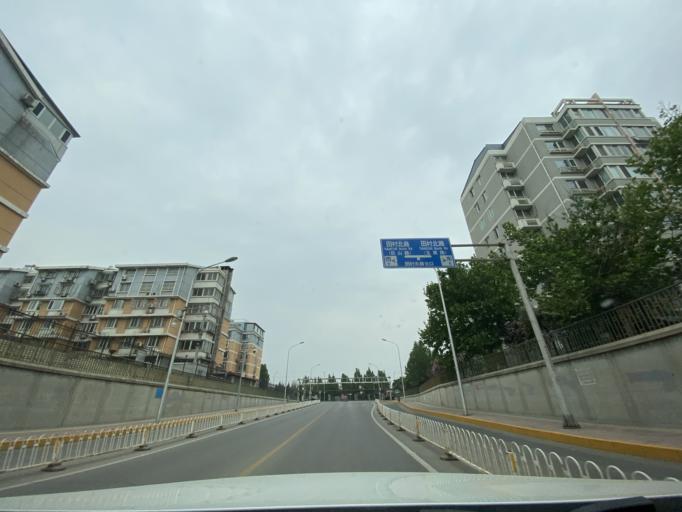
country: CN
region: Beijing
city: Sijiqing
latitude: 39.9318
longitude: 116.2422
